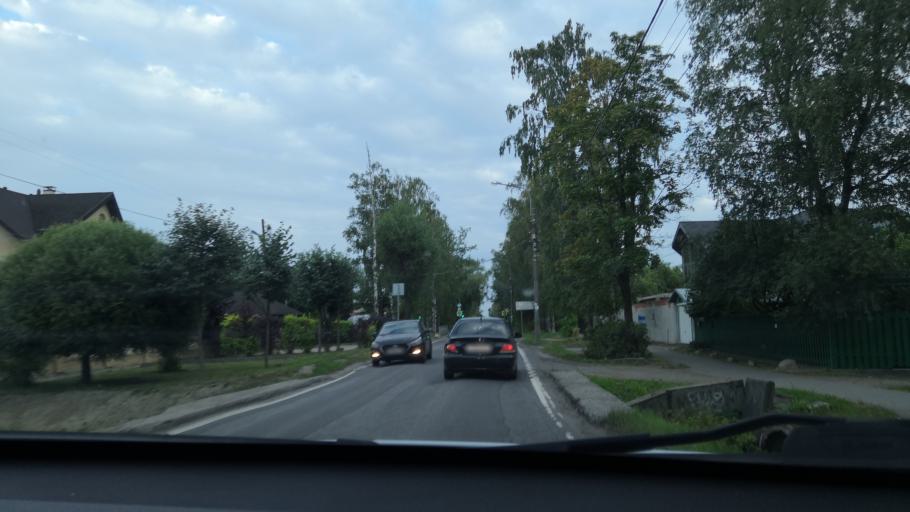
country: RU
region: St.-Petersburg
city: Pushkin
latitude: 59.7004
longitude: 30.4091
